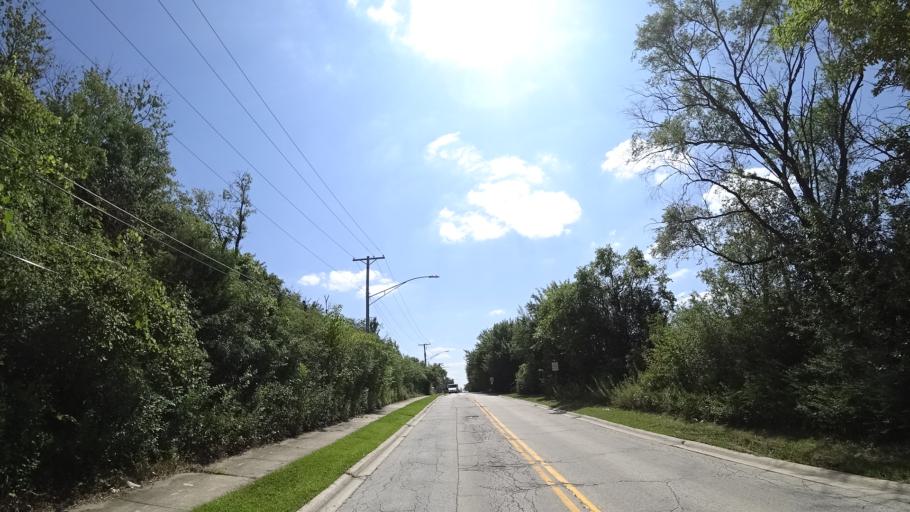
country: US
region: Illinois
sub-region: Cook County
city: Orland Park
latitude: 41.6279
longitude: -87.8488
